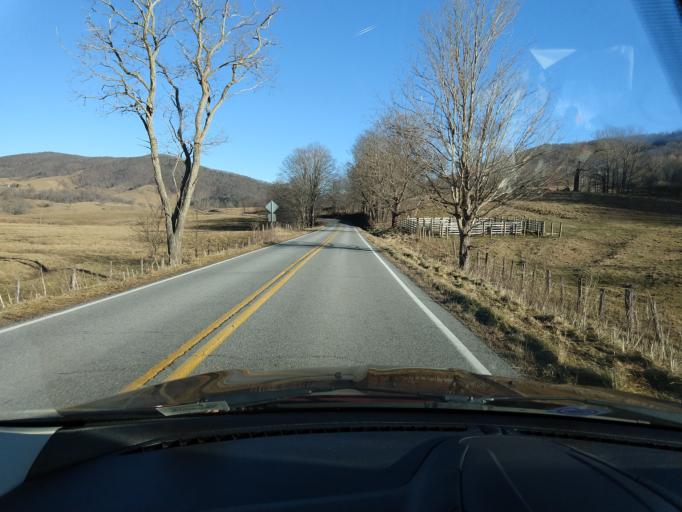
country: US
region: Virginia
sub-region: Highland County
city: Monterey
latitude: 38.3760
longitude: -79.6636
